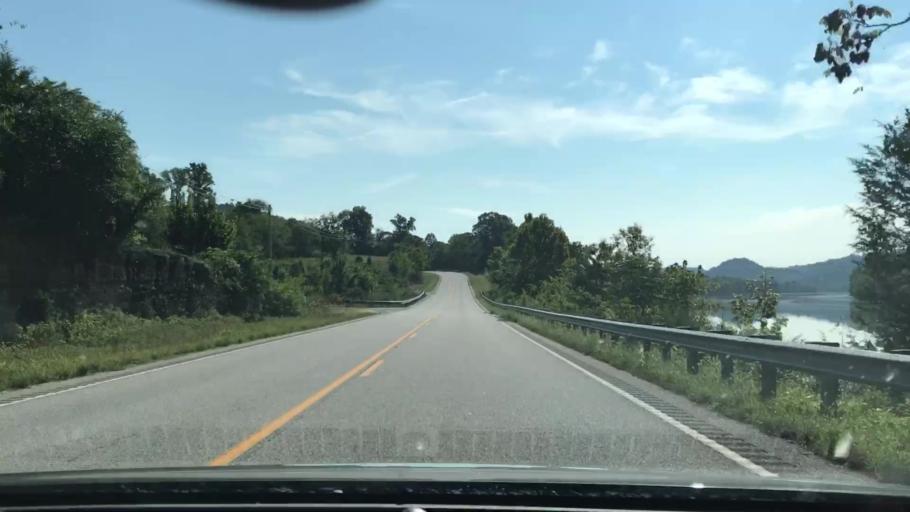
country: US
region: Tennessee
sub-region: Jackson County
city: Gainesboro
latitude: 36.3590
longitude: -85.7455
